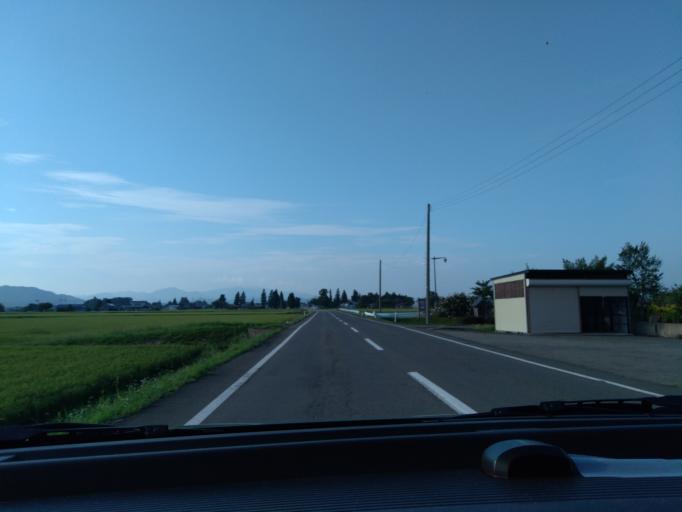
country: JP
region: Akita
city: Kakunodatemachi
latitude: 39.5060
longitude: 140.5596
